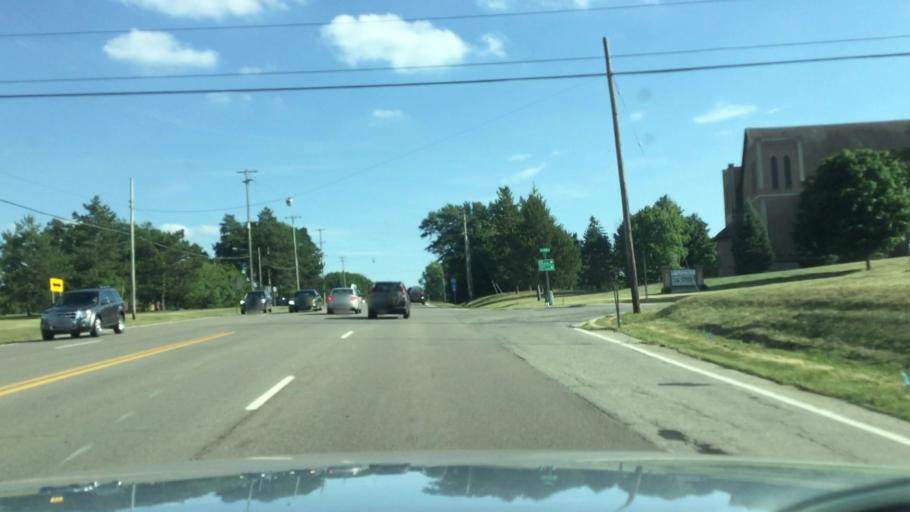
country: US
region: Michigan
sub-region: Genesee County
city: Grand Blanc
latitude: 42.9021
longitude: -83.6025
